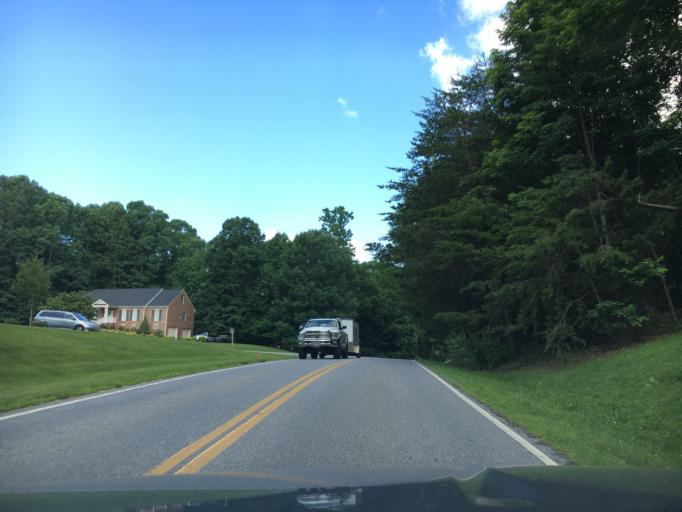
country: US
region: Virginia
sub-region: Bedford County
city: Forest
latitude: 37.3852
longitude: -79.2603
